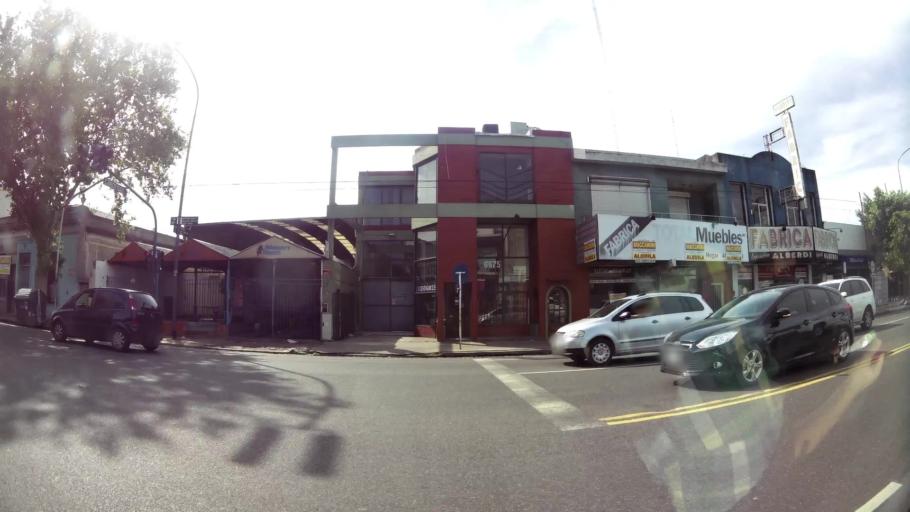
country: AR
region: Buenos Aires F.D.
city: Villa Lugano
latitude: -34.6570
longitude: -58.5091
